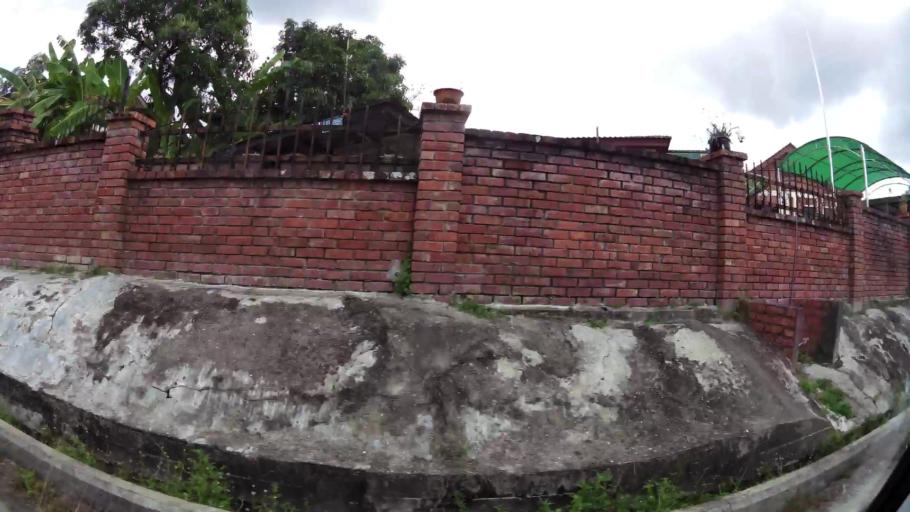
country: BN
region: Brunei and Muara
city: Bandar Seri Begawan
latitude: 4.9523
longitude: 114.9582
